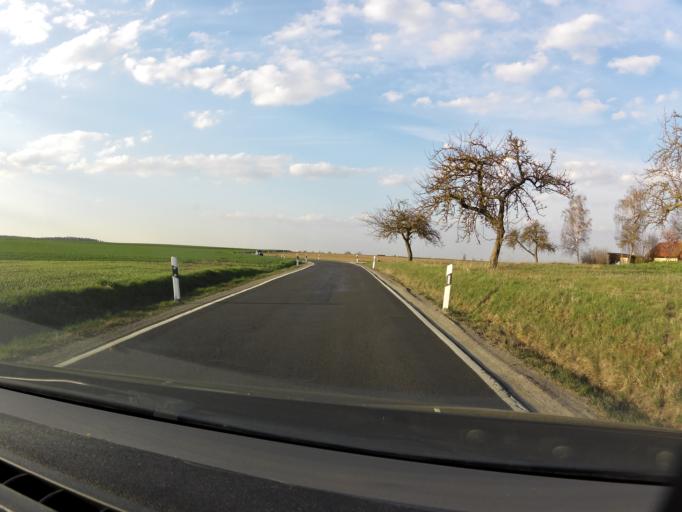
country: DE
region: Bavaria
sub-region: Regierungsbezirk Unterfranken
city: Geroldshausen
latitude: 49.6929
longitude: 9.9045
